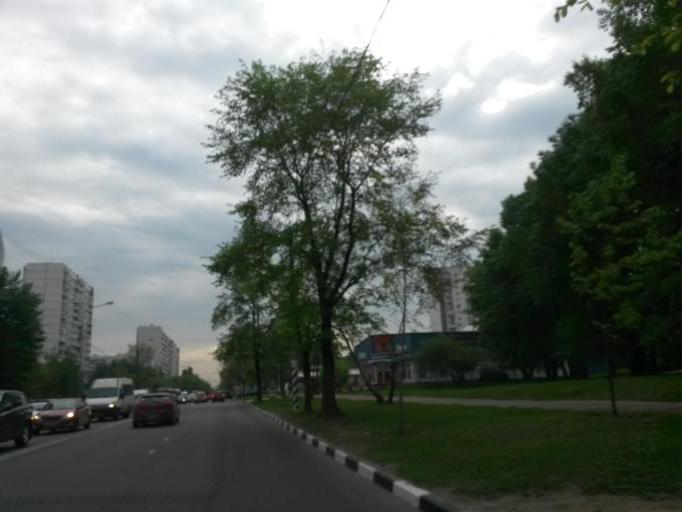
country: RU
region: Moscow
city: Orekhovo-Borisovo
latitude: 55.6245
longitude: 37.7126
